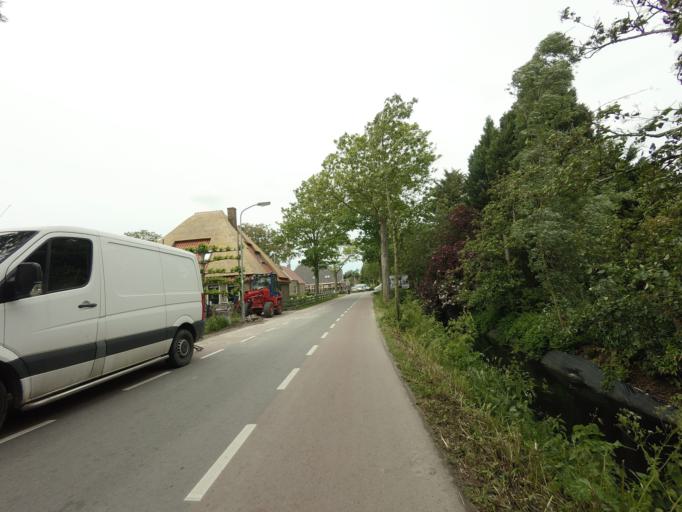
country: NL
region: North Holland
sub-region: Gemeente Hoorn
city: Hoorn
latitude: 52.6459
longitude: 5.1226
